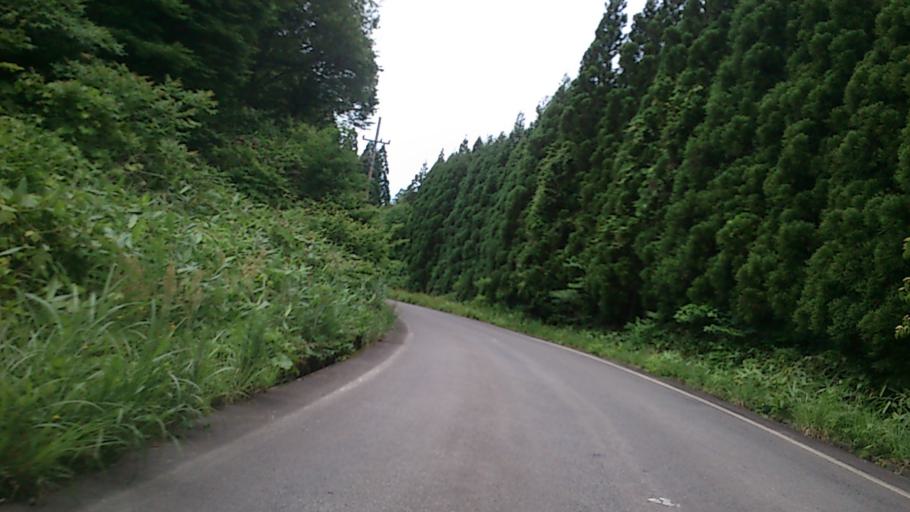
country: JP
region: Yamagata
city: Yuza
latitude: 39.0930
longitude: 139.9136
